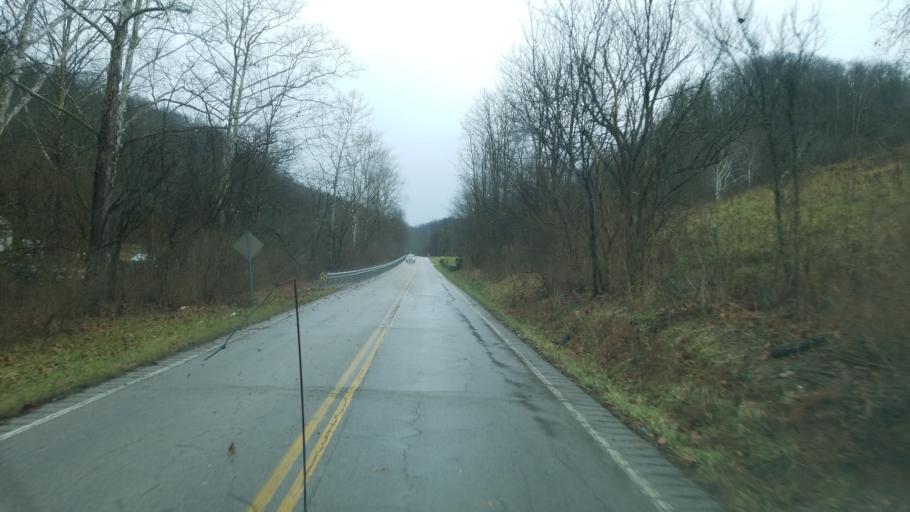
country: US
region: Kentucky
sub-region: Mason County
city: Maysville
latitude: 38.6257
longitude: -83.7052
